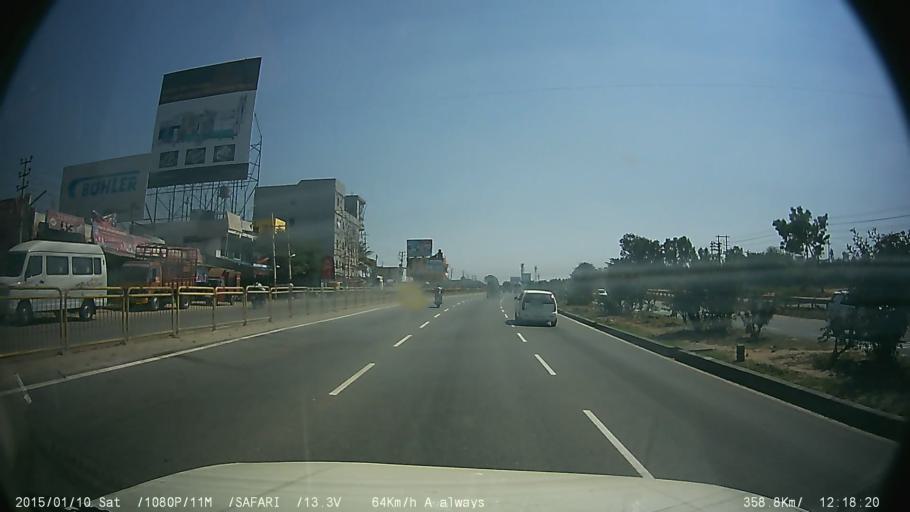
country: IN
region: Karnataka
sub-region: Bangalore Urban
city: Anekal
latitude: 12.7917
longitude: 77.7303
